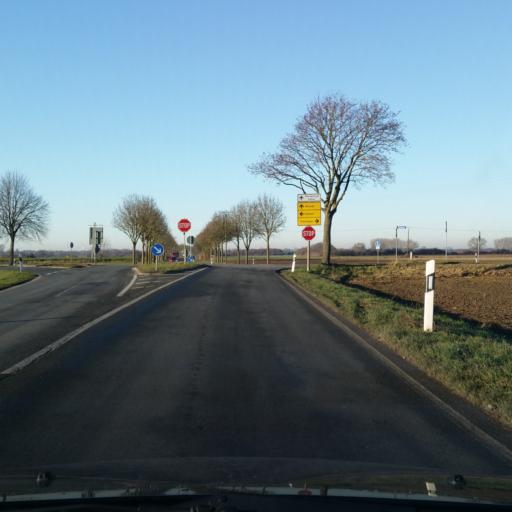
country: DE
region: North Rhine-Westphalia
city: Kalkar
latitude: 51.7429
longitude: 6.3288
